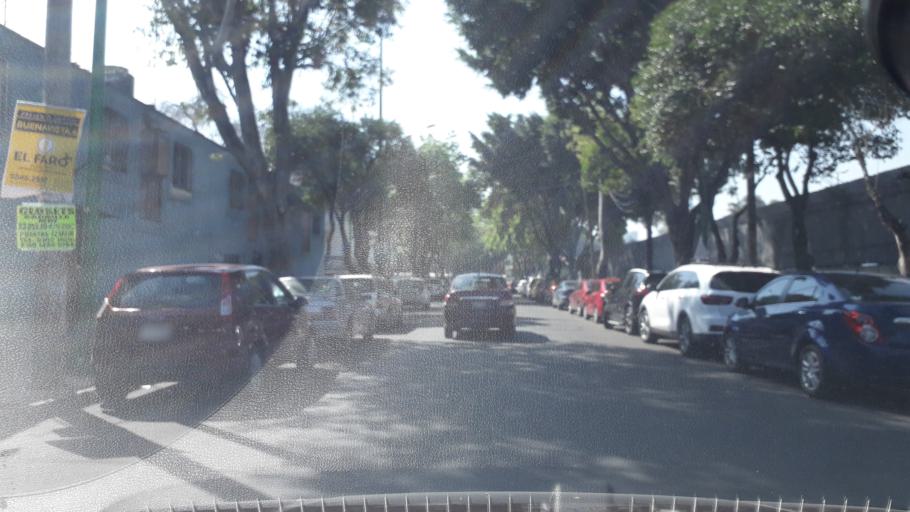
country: MX
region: Mexico City
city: Cuauhtemoc
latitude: 19.4453
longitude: -99.1508
